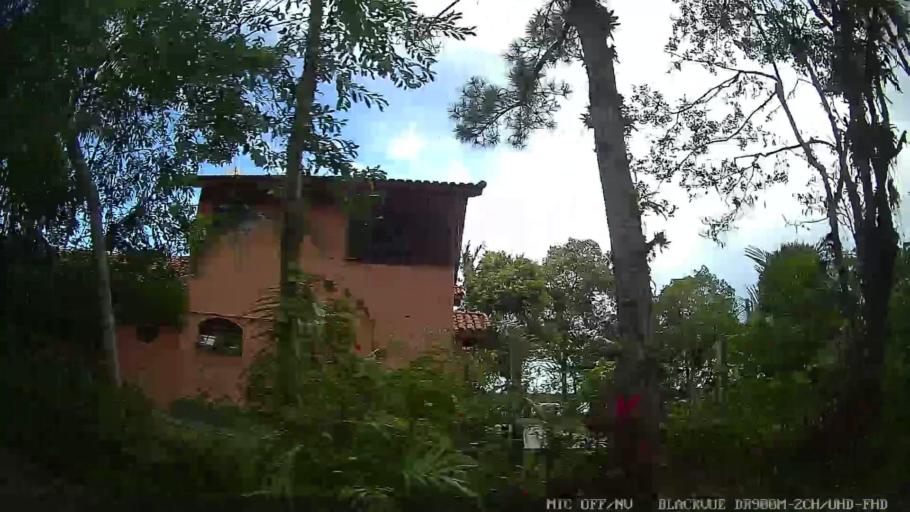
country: BR
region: Sao Paulo
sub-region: Iguape
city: Iguape
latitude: -24.6893
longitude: -47.5207
